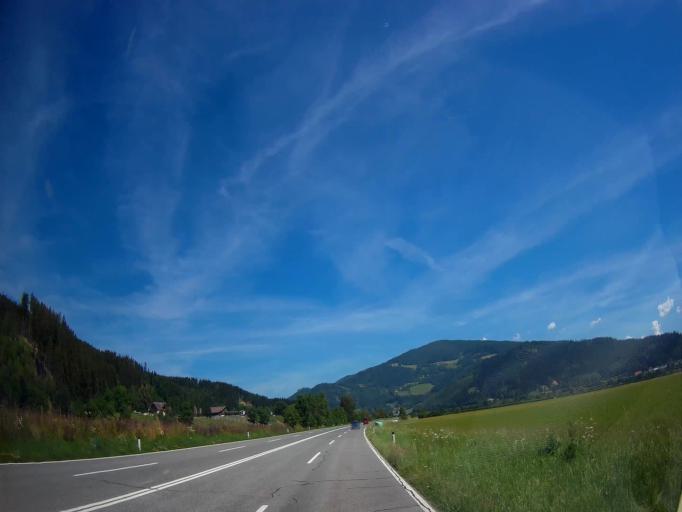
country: AT
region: Carinthia
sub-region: Politischer Bezirk Sankt Veit an der Glan
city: Molbling
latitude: 46.8674
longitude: 14.4488
